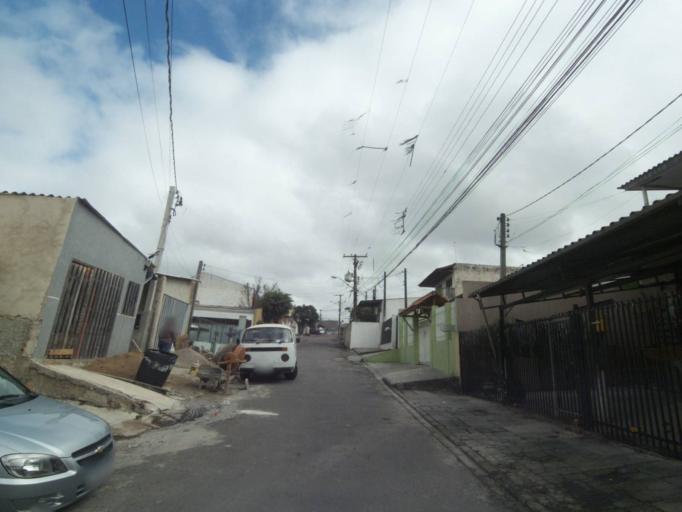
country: BR
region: Parana
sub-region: Sao Jose Dos Pinhais
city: Sao Jose dos Pinhais
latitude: -25.5327
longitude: -49.2879
